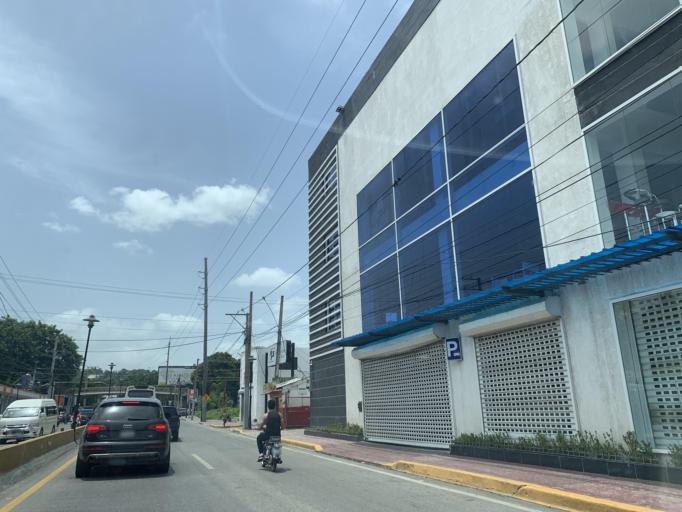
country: DO
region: Puerto Plata
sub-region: Puerto Plata
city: Puerto Plata
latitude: 19.7887
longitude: -70.6979
